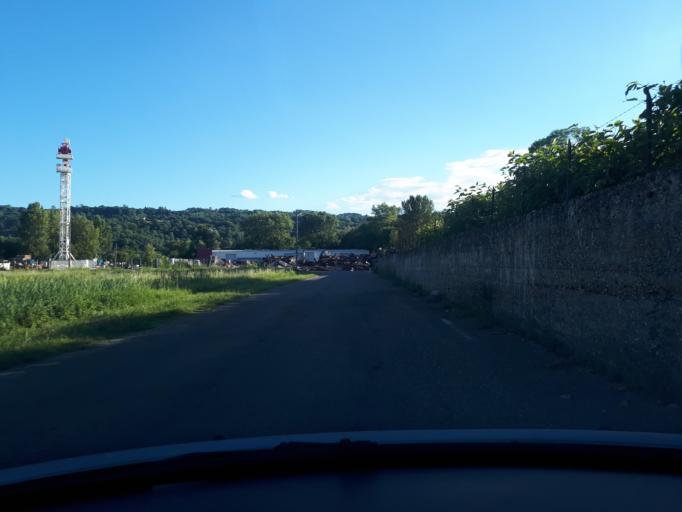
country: FR
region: Rhone-Alpes
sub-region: Departement de l'Isere
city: Bourgoin-Jallieu
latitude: 45.5937
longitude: 5.2621
